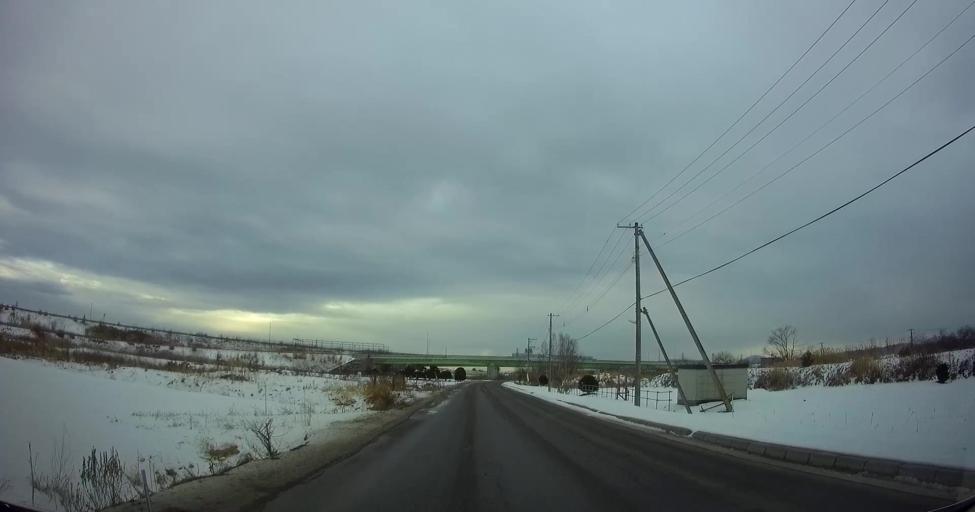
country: JP
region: Hokkaido
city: Nanae
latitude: 41.8362
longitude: 140.6915
